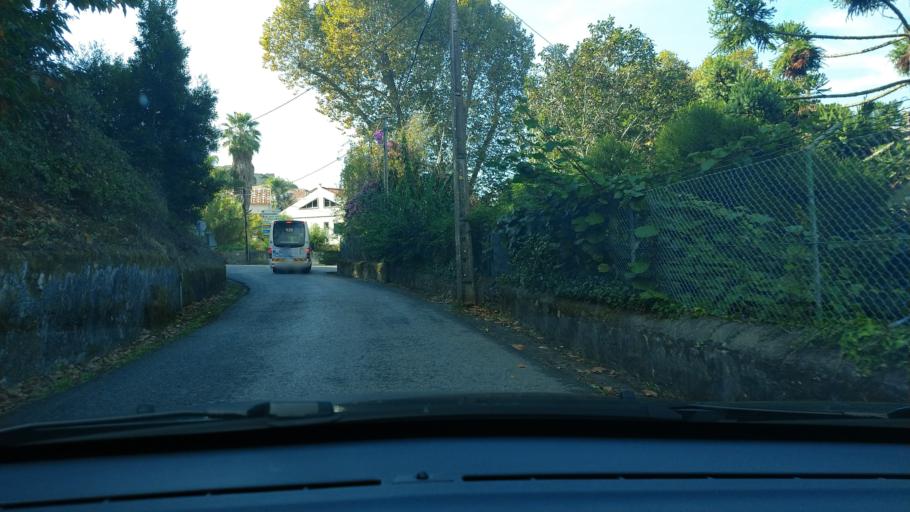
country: PT
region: Lisbon
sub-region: Sintra
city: Colares
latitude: 38.7988
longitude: -9.4438
